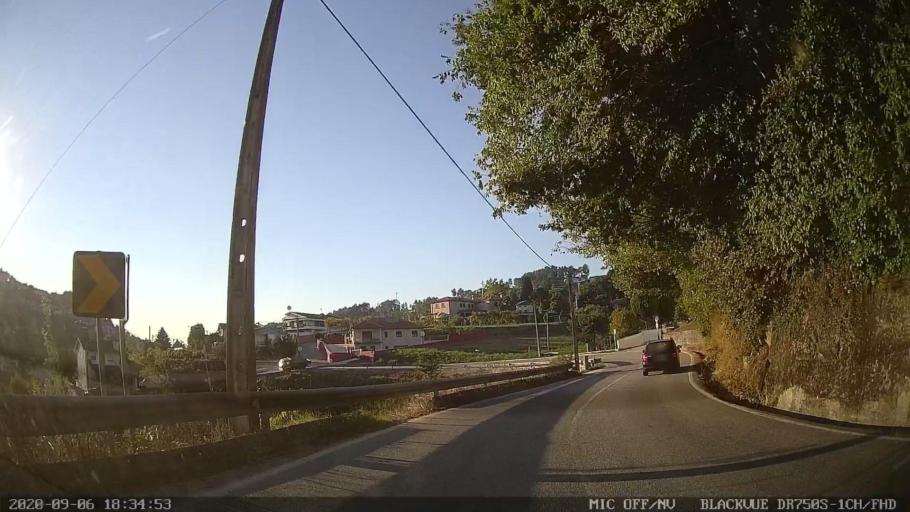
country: PT
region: Porto
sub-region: Amarante
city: Amarante
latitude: 41.2550
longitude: -8.0514
